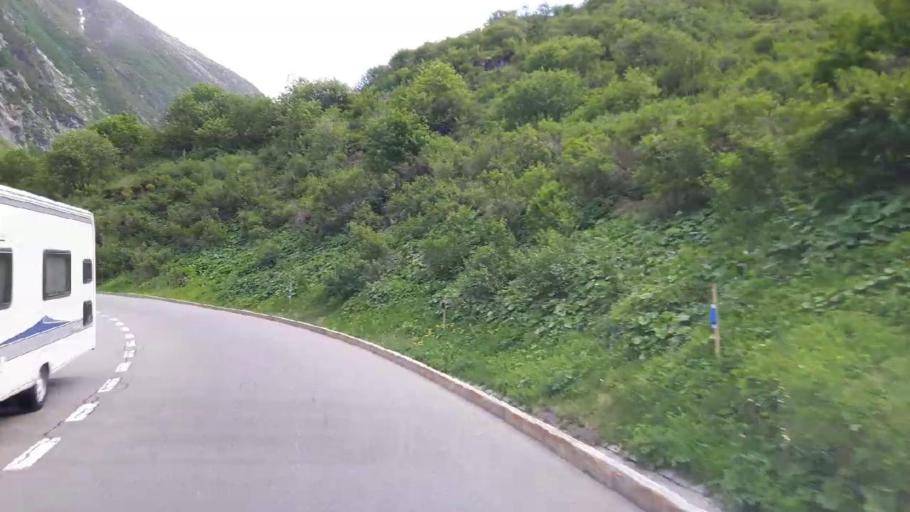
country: CH
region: Uri
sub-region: Uri
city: Andermatt
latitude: 46.6144
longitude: 8.5709
